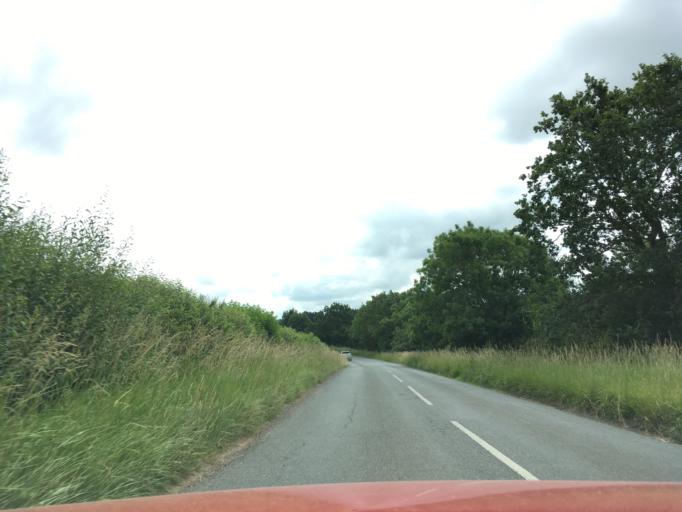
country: GB
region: England
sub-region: Oxfordshire
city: Shipton under Wychwood
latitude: 51.9019
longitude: -1.6175
